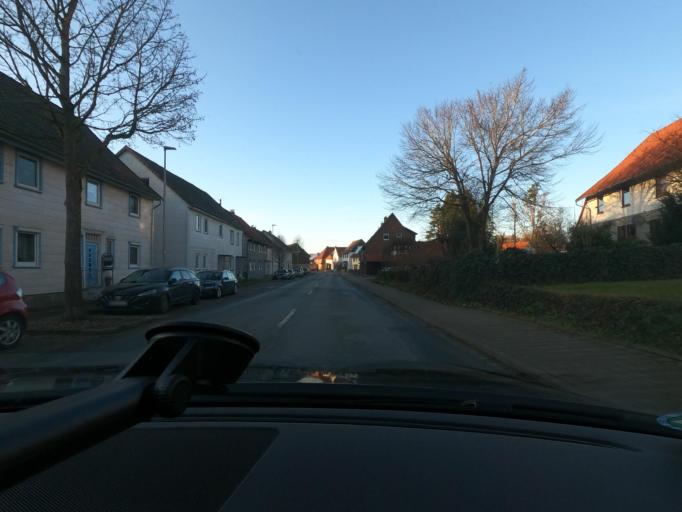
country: DE
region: Lower Saxony
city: Badenhausen
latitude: 51.7672
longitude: 10.2082
